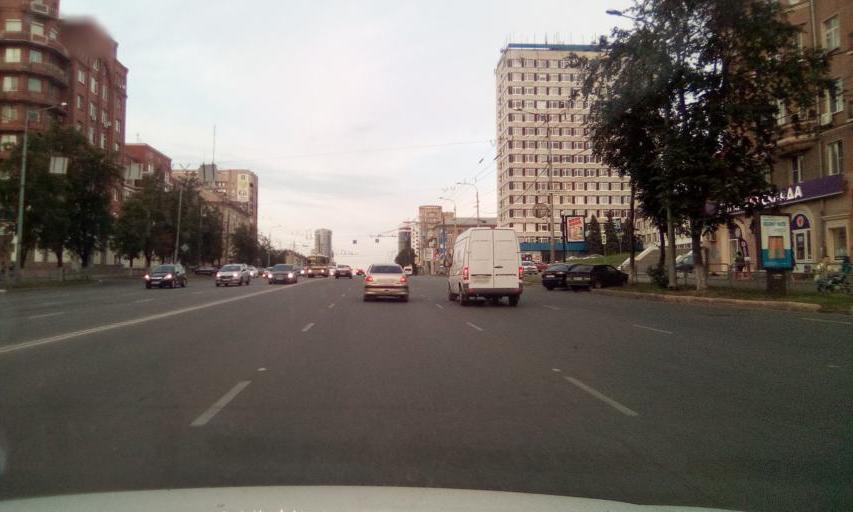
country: RU
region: Chelyabinsk
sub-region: Gorod Chelyabinsk
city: Chelyabinsk
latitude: 55.1605
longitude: 61.4130
